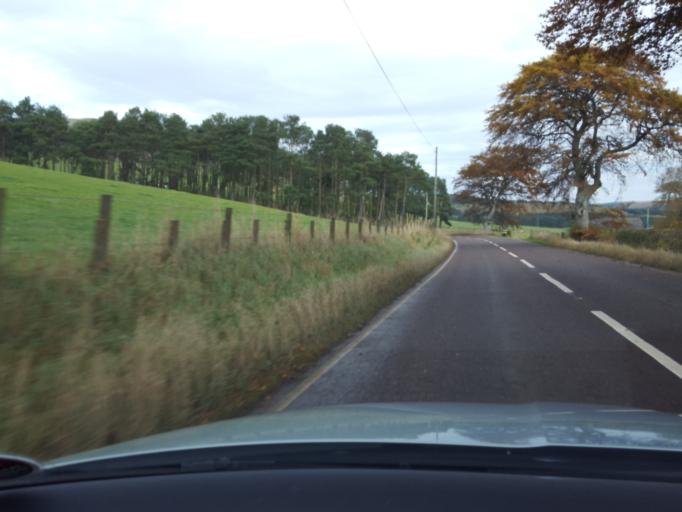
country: GB
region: Scotland
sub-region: South Lanarkshire
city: Biggar
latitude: 55.6804
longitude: -3.4792
